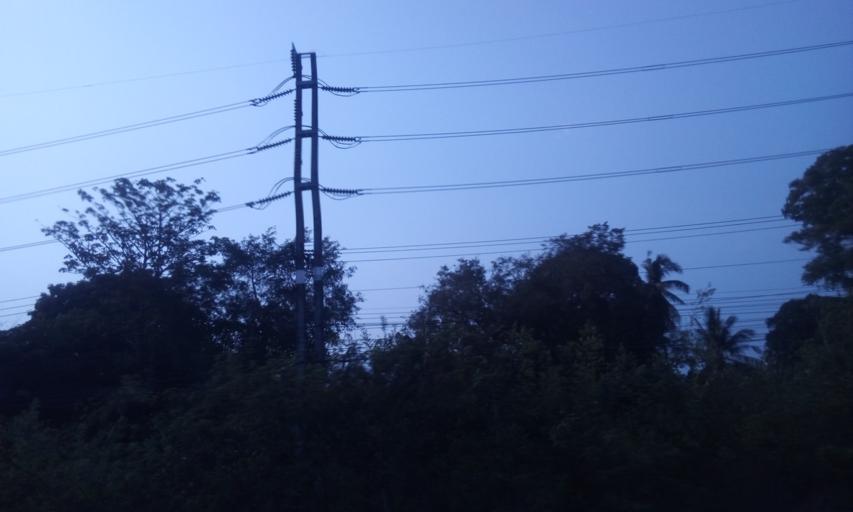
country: TH
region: Chanthaburi
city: Khlung
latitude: 12.4544
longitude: 102.2580
